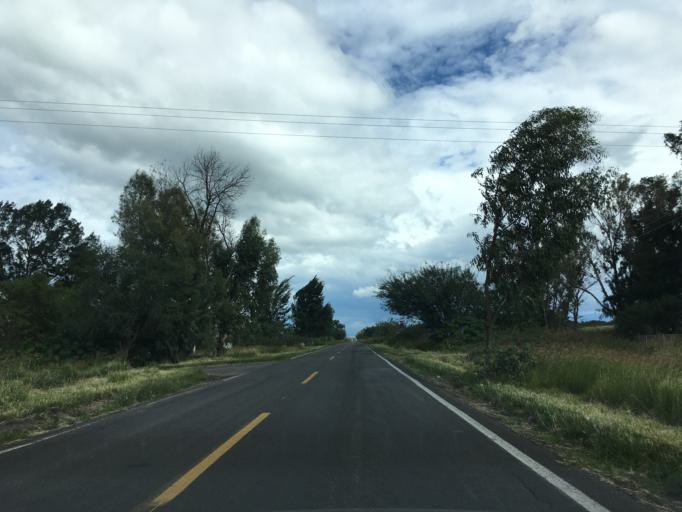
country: MX
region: Michoacan
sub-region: Cuitzeo
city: Cuamio
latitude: 20.0539
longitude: -101.0893
